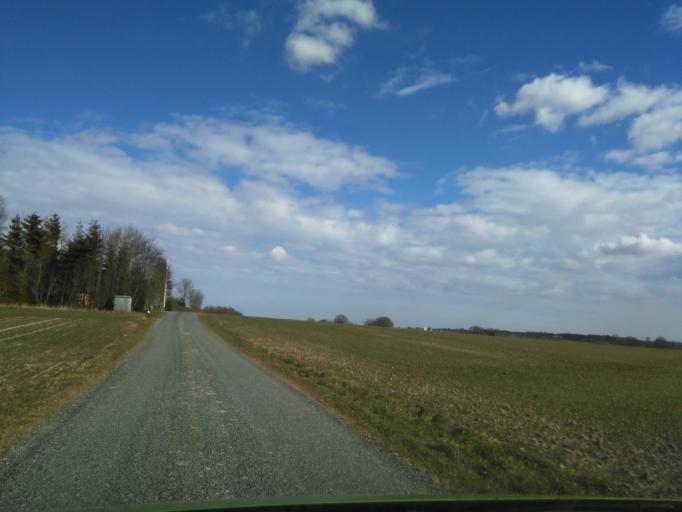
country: DK
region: Central Jutland
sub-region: Arhus Kommune
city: Solbjerg
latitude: 55.9200
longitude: 10.0129
